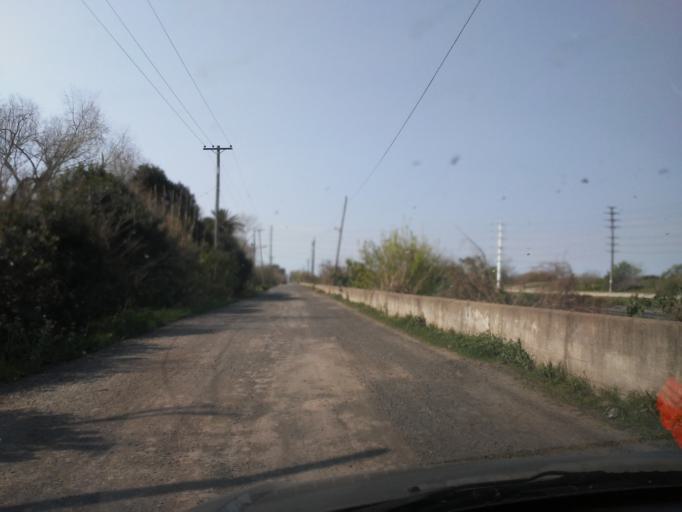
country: AR
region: Buenos Aires
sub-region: Partido de Avellaneda
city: Avellaneda
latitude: -34.6767
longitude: -58.3110
